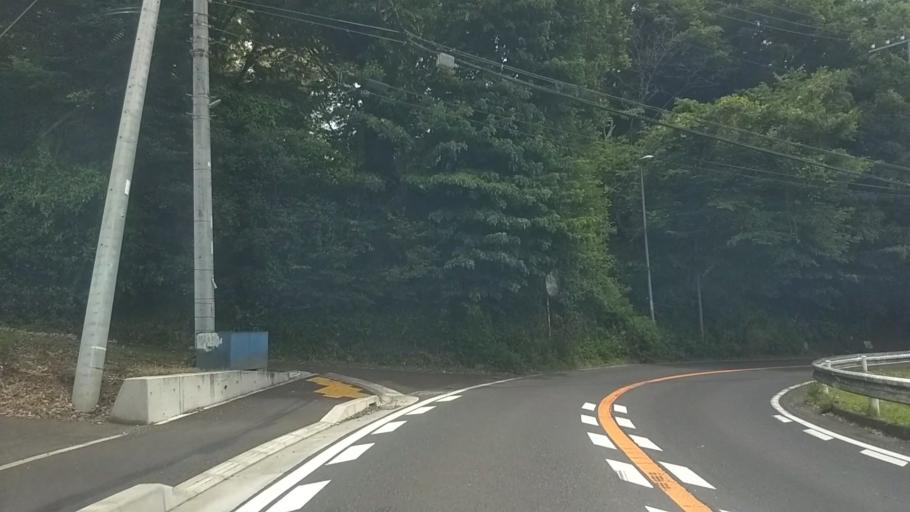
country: JP
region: Kanagawa
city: Chigasaki
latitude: 35.3681
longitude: 139.4220
